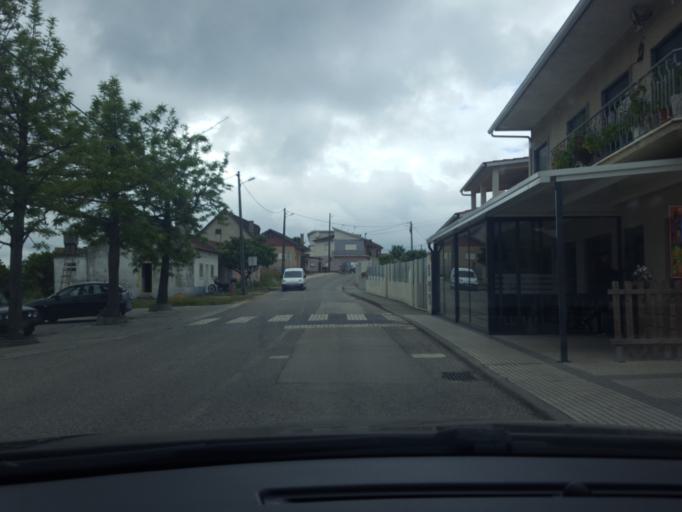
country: PT
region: Leiria
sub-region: Leiria
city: Caranguejeira
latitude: 39.7954
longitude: -8.7530
